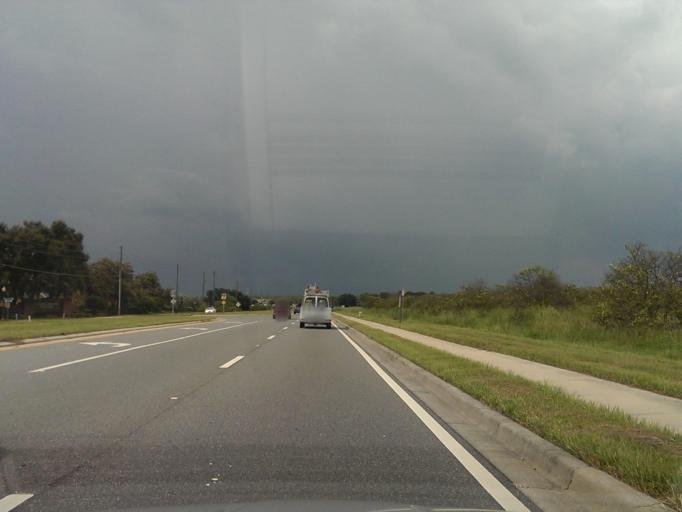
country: US
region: Florida
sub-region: Orange County
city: Lake Butler
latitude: 28.4803
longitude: -81.5825
